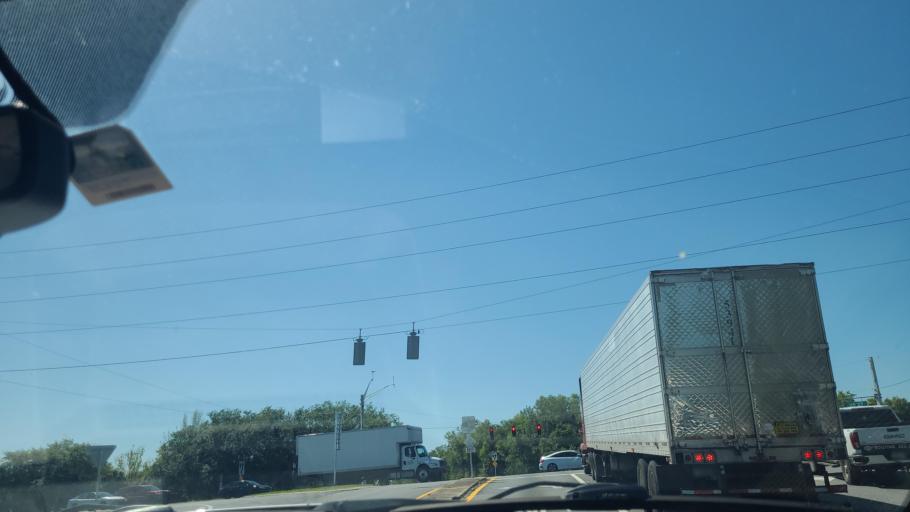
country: US
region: Florida
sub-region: Lake County
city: Howie In The Hills
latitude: 28.6435
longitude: -81.8092
